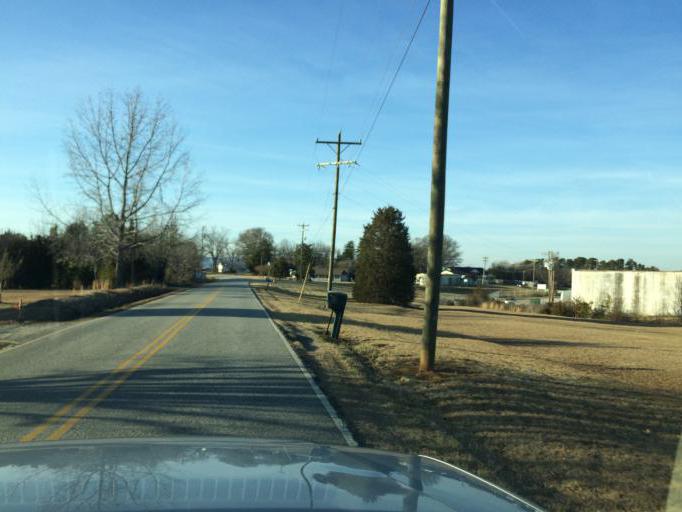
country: US
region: South Carolina
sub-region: Spartanburg County
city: Landrum
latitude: 35.1441
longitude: -82.1028
